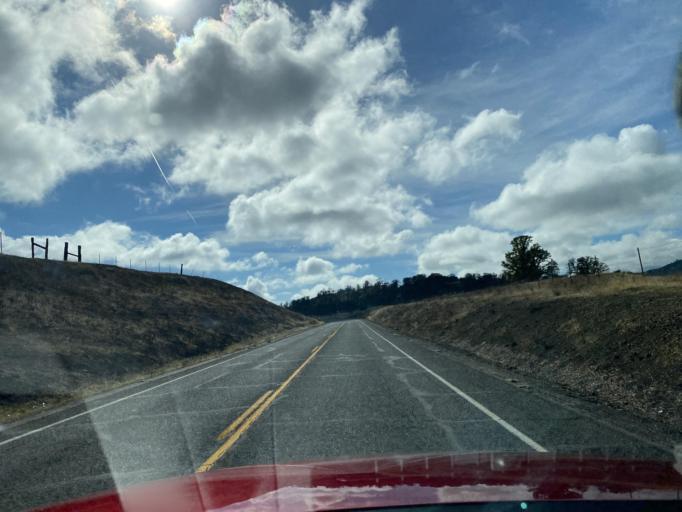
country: US
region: California
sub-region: Glenn County
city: Willows
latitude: 39.5408
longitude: -122.5354
